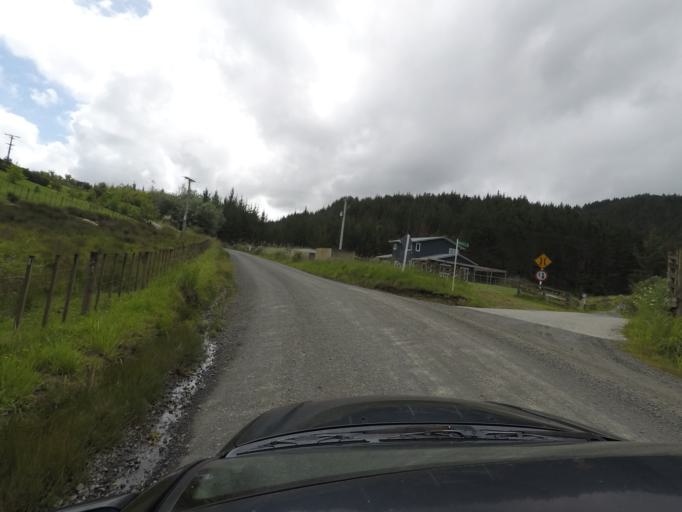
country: NZ
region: Auckland
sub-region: Auckland
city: Warkworth
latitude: -36.4898
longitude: 174.6210
